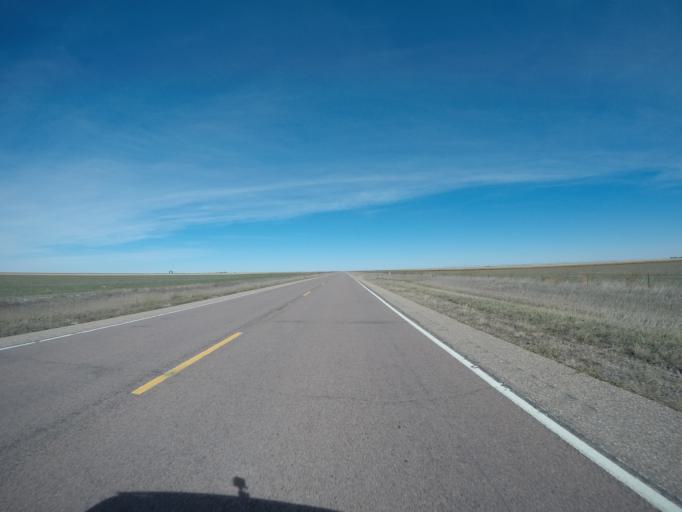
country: US
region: Colorado
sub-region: Kit Carson County
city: Burlington
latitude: 39.6757
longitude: -102.4160
